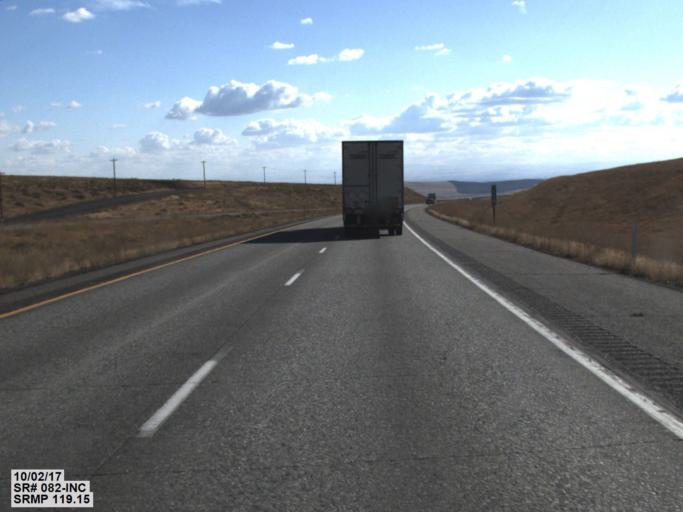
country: US
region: Washington
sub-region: Benton County
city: Highland
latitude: 46.0775
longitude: -119.2222
